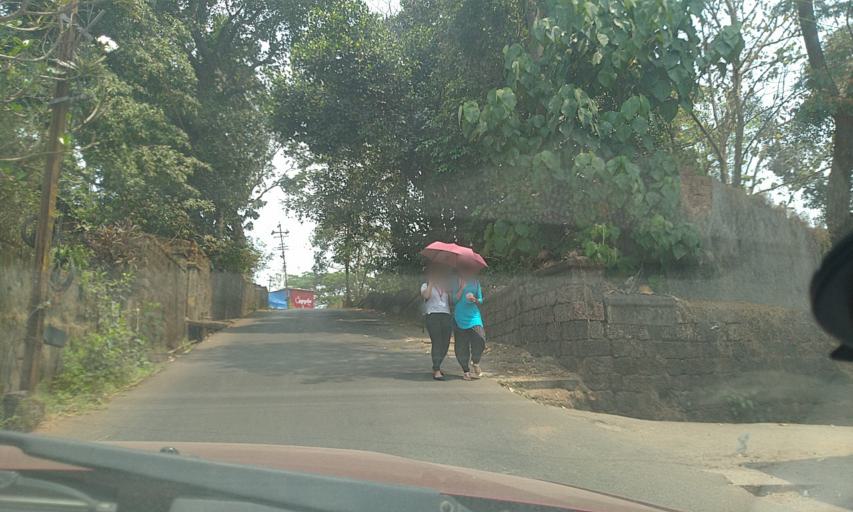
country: IN
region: Goa
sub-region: North Goa
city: Mapuca
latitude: 15.5959
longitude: 73.8099
